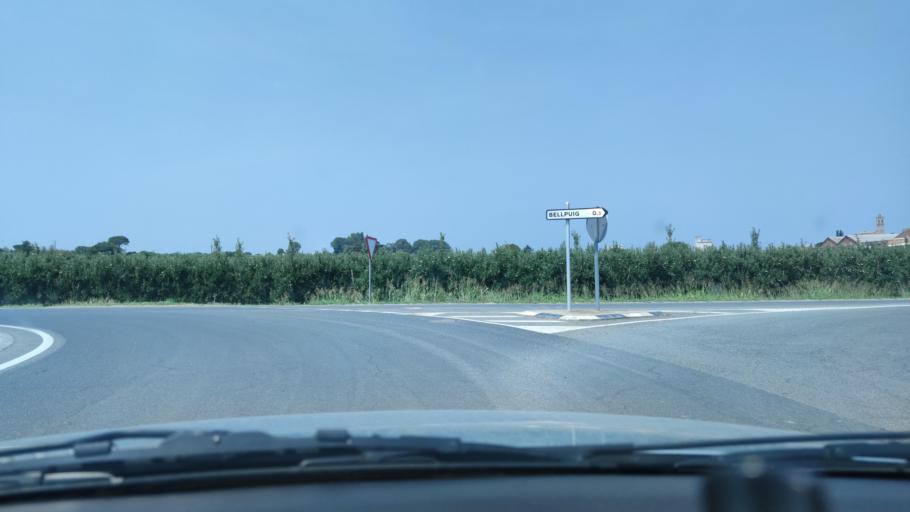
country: ES
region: Catalonia
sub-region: Provincia de Lleida
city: Bellpuig
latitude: 41.6191
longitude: 1.0208
